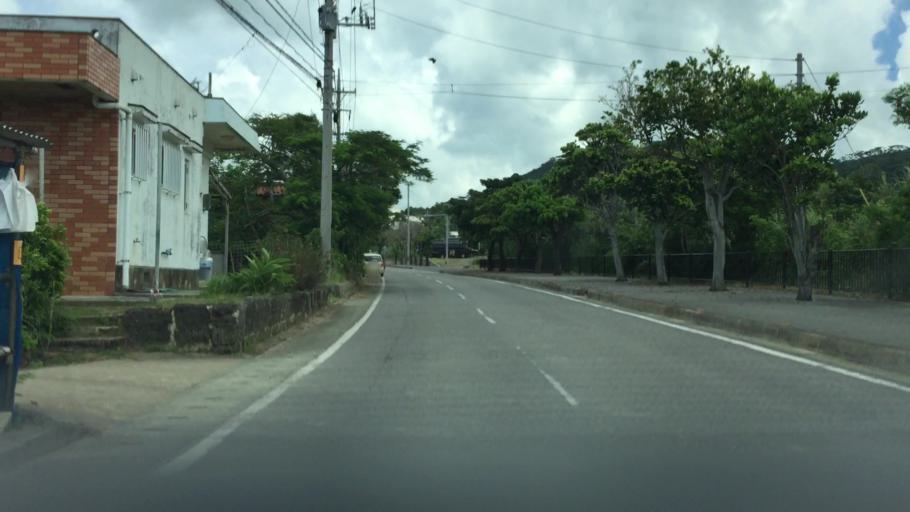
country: JP
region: Okinawa
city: Ishigaki
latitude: 24.3629
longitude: 124.1428
